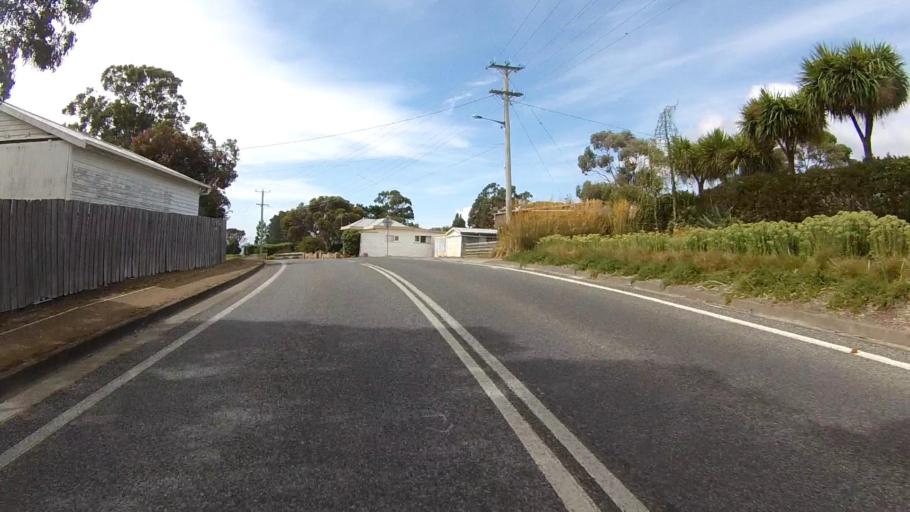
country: AU
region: Tasmania
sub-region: Kingborough
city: Kettering
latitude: -43.1568
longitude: 147.2383
